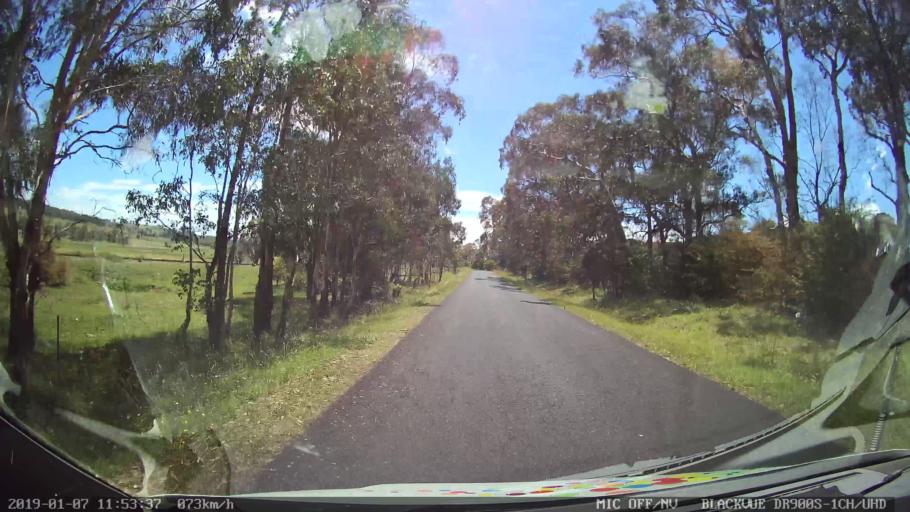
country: AU
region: New South Wales
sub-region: Guyra
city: Guyra
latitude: -30.3031
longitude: 151.6592
